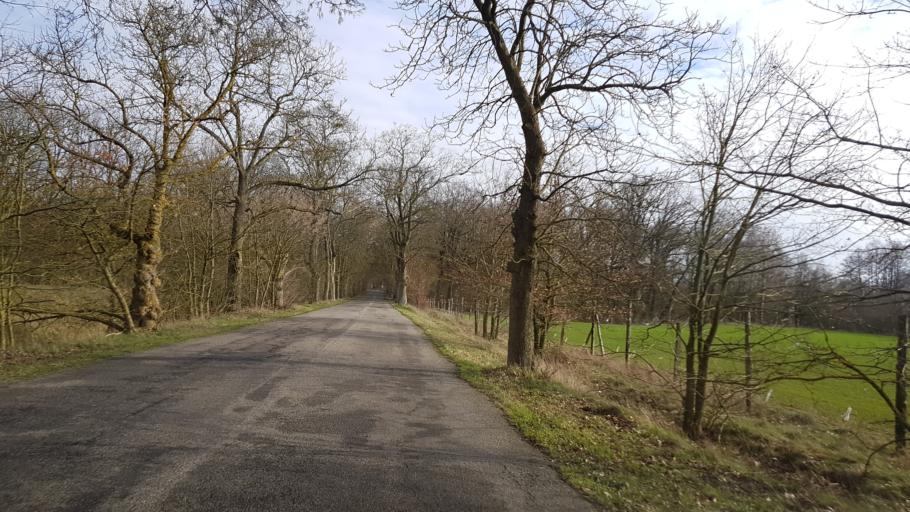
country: PL
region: West Pomeranian Voivodeship
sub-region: Powiat policki
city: Dobra
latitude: 53.5391
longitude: 14.3157
